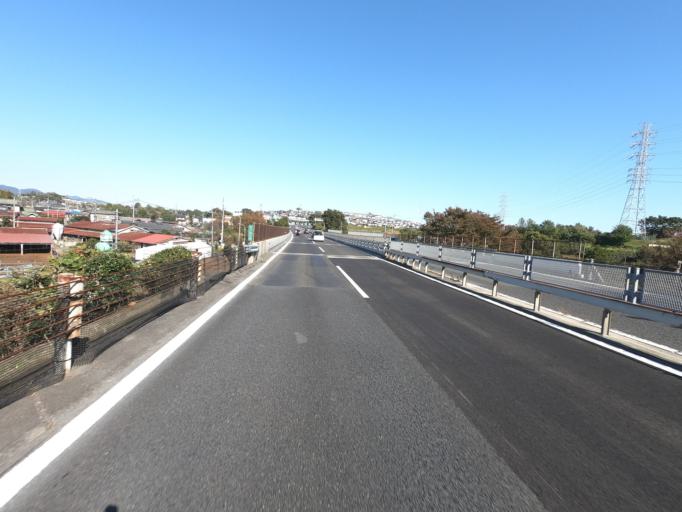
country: JP
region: Kanagawa
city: Oiso
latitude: 35.3331
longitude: 139.2932
